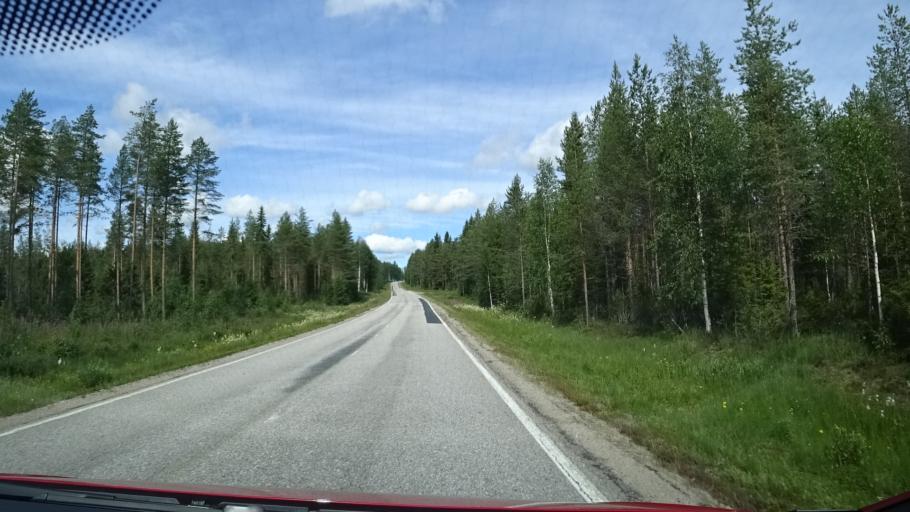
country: FI
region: Kainuu
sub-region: Kehys-Kainuu
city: Kuhmo
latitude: 64.4624
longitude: 29.7603
